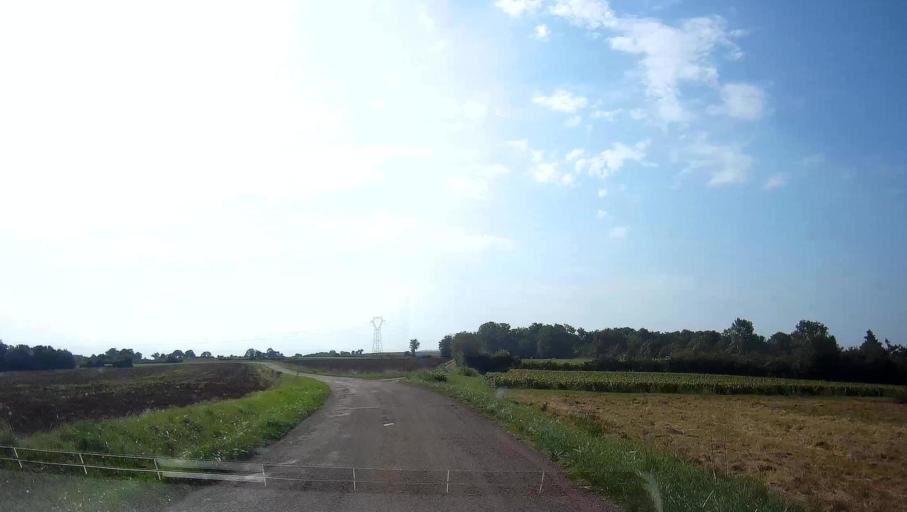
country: FR
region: Bourgogne
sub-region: Departement de Saone-et-Loire
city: Couches
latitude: 46.8958
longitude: 4.6037
